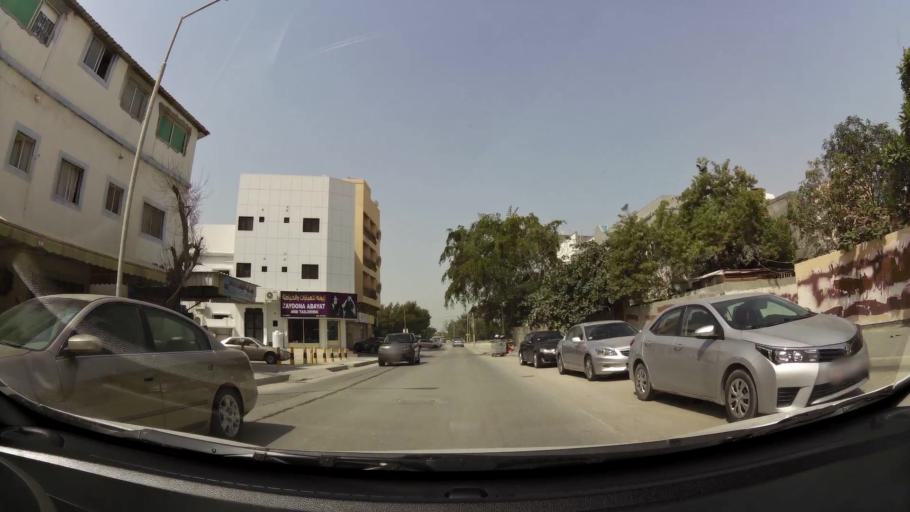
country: BH
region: Manama
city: Jidd Hafs
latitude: 26.2306
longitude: 50.5067
